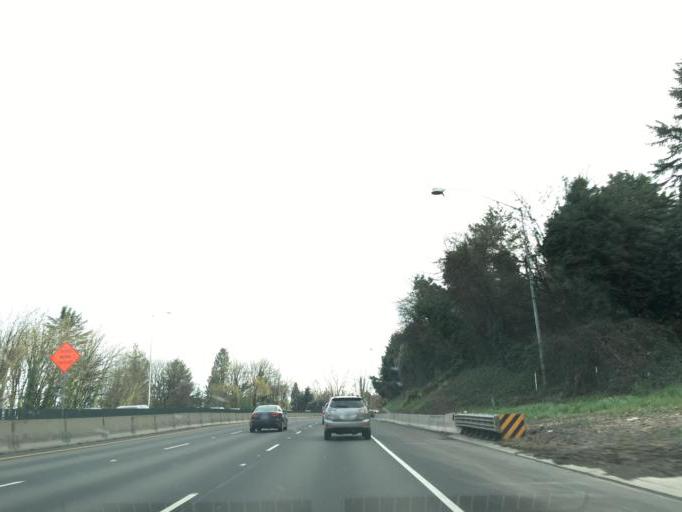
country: US
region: Oregon
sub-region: Clackamas County
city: Milwaukie
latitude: 45.4733
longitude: -122.6781
